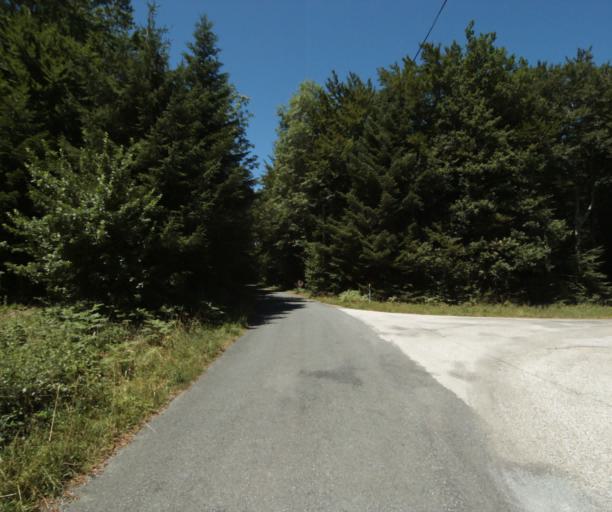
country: FR
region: Languedoc-Roussillon
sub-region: Departement de l'Aude
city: Cuxac-Cabardes
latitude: 43.3993
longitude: 2.2207
